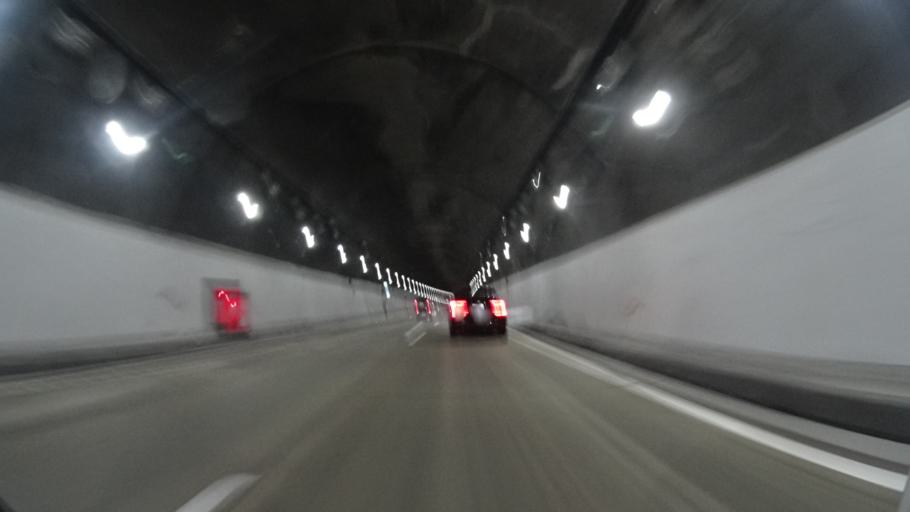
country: JP
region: Ehime
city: Kawanoecho
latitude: 34.0342
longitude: 133.6039
